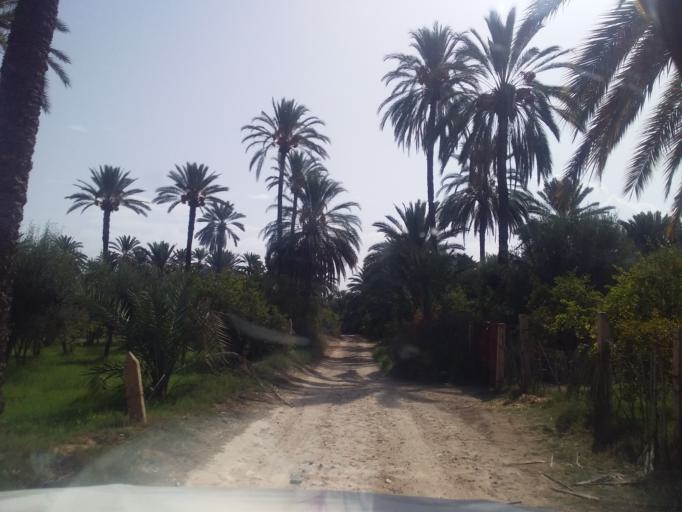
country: TN
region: Qabis
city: Gabes
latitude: 33.6269
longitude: 10.2887
